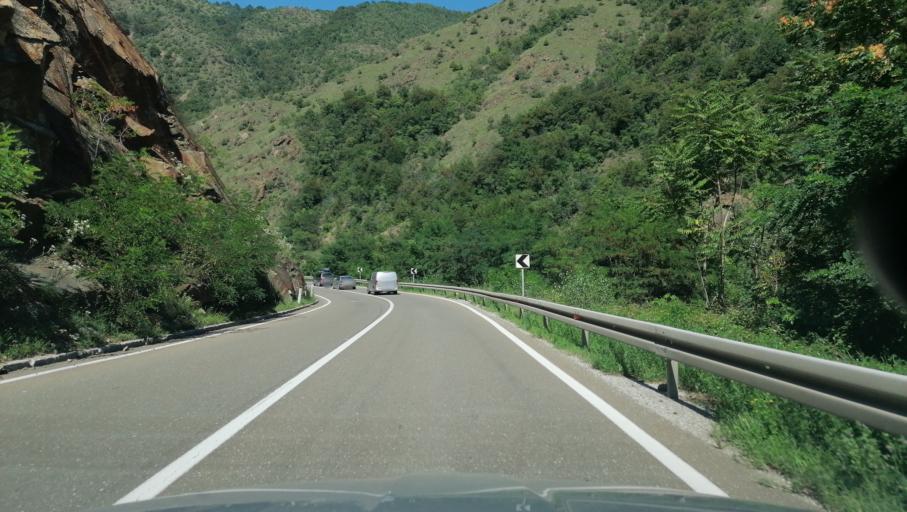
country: RS
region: Central Serbia
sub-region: Raski Okrug
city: Kraljevo
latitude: 43.5854
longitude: 20.5805
